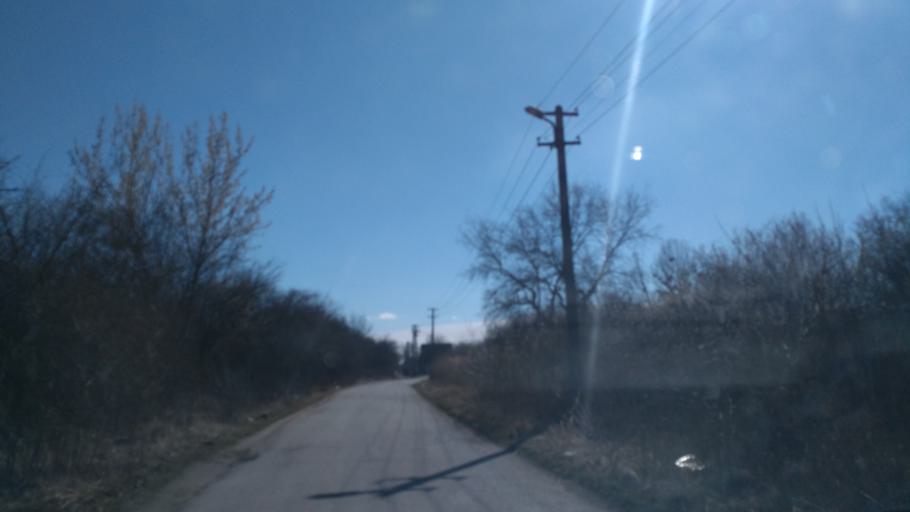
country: SK
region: Kosicky
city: Kosice
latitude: 48.6003
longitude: 21.3126
